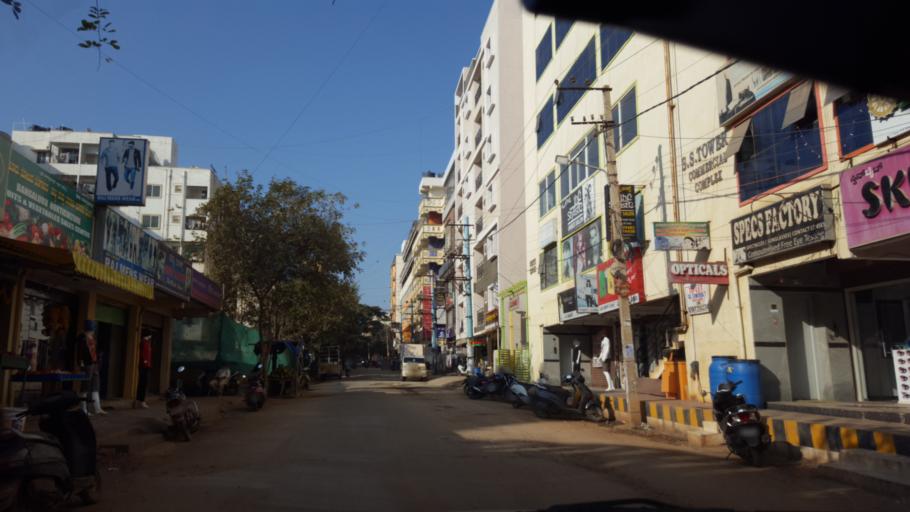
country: IN
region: Karnataka
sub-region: Bangalore Urban
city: Bangalore
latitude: 12.9500
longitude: 77.7155
